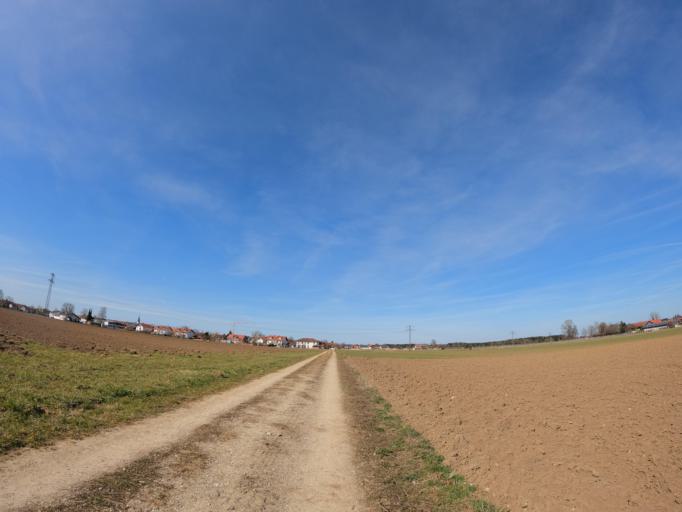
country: DE
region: Bavaria
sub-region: Upper Bavaria
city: Brunnthal
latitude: 48.0031
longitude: 11.6898
